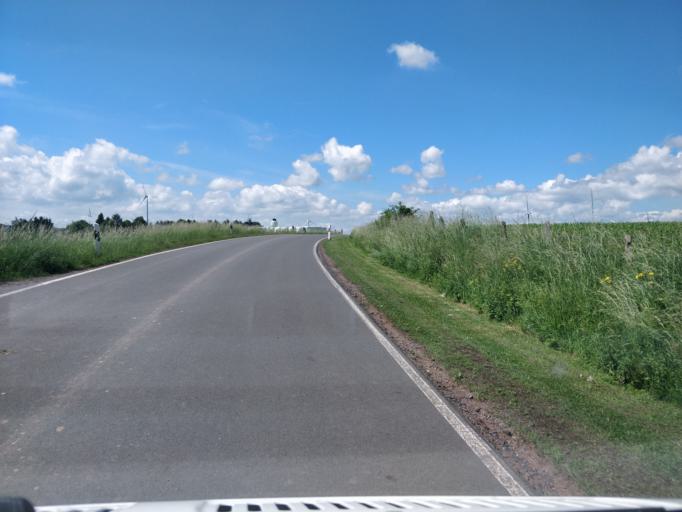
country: DE
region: Rheinland-Pfalz
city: Scheid
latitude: 50.3632
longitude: 6.4203
